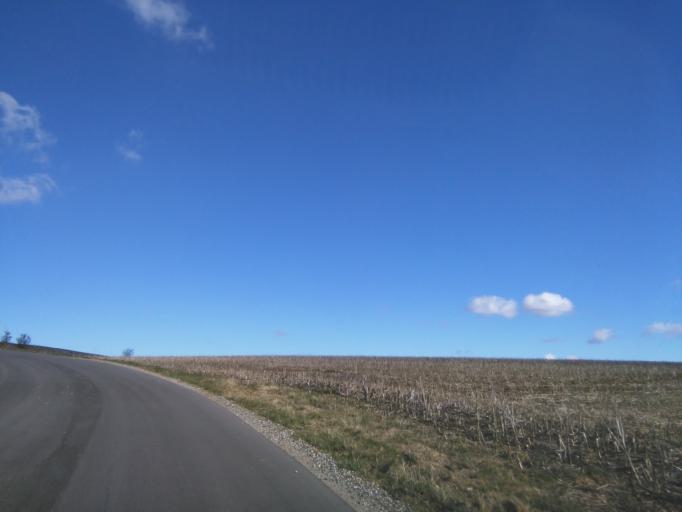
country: DK
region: Central Jutland
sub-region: Skanderborg Kommune
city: Ry
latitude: 56.1290
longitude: 9.7375
